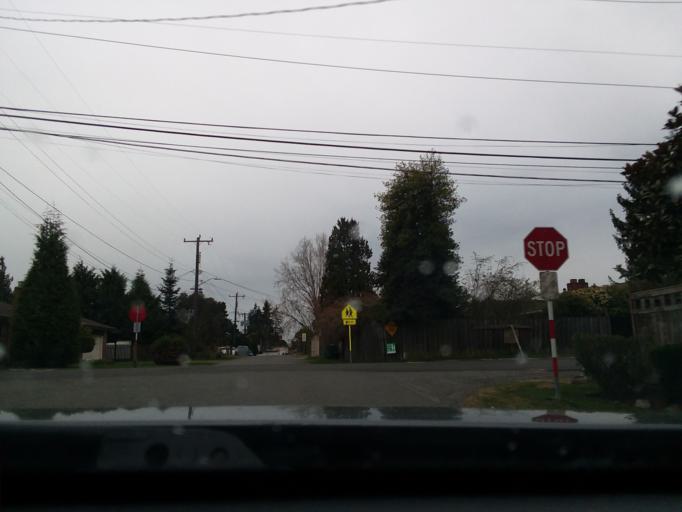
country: US
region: Washington
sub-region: King County
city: Shoreline
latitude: 47.6992
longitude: -122.3786
